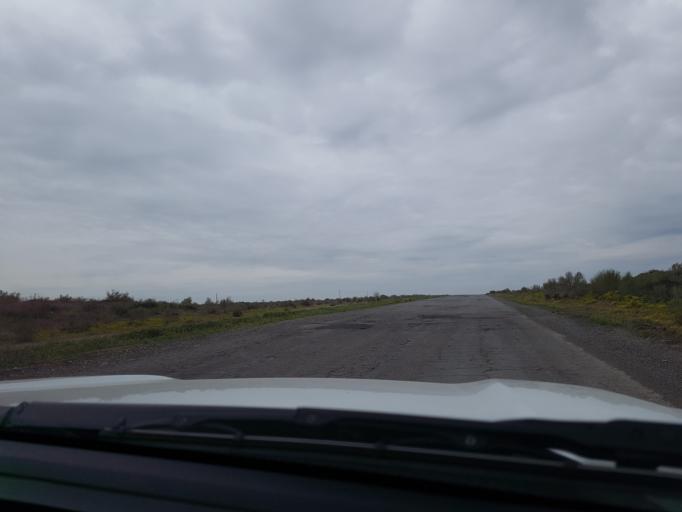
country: TM
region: Mary
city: Bayramaly
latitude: 37.9125
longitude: 62.6213
